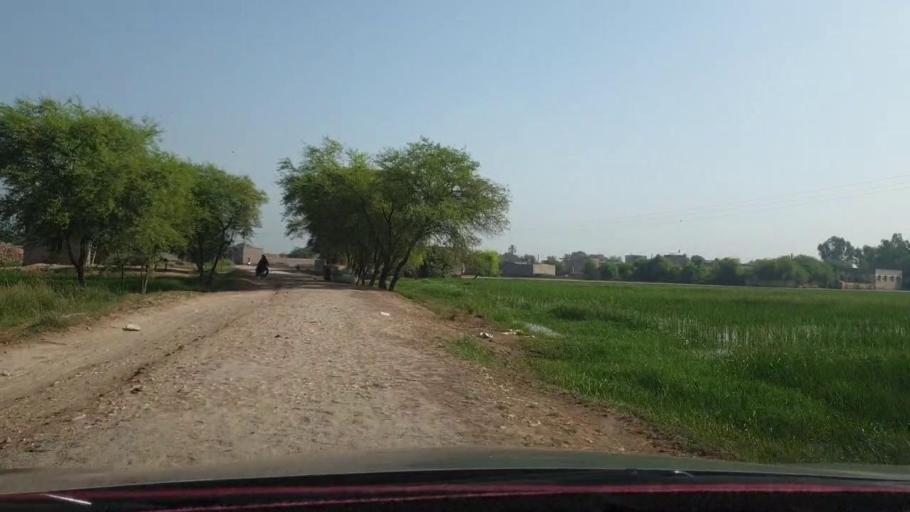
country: PK
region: Sindh
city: Nasirabad
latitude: 27.4598
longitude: 67.9185
